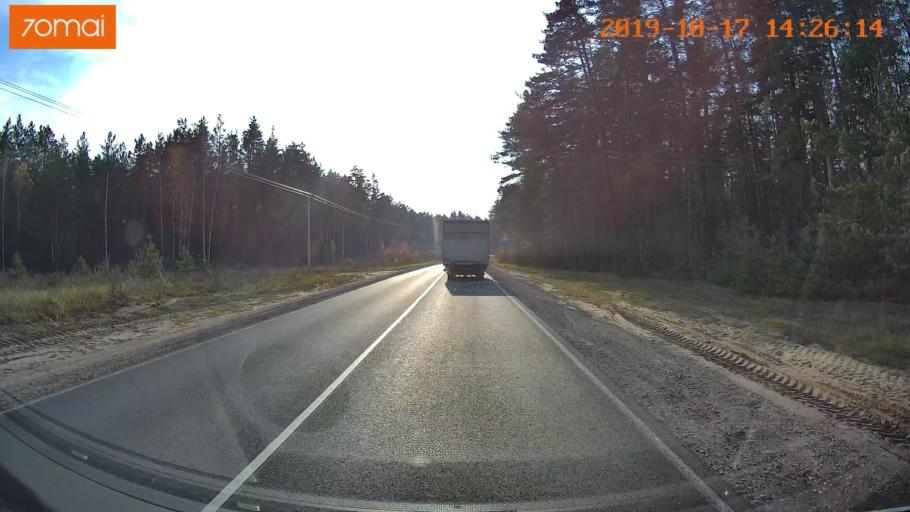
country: RU
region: Moskovskaya
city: Radovitskiy
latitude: 54.9936
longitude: 39.9695
